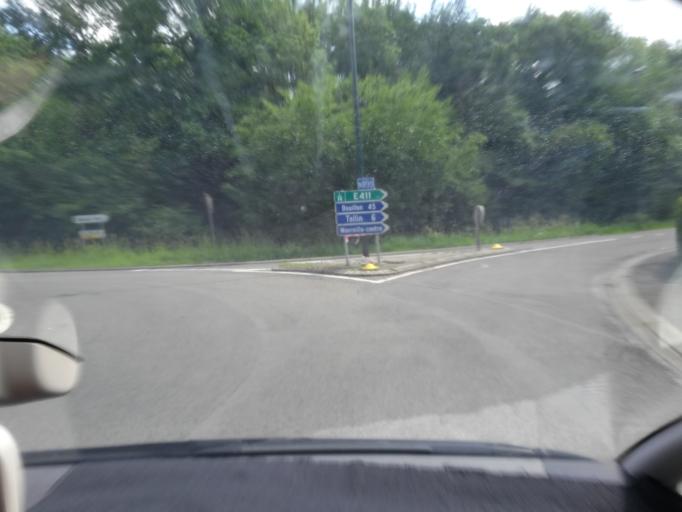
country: BE
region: Wallonia
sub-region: Province de Namur
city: Rochefort
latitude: 50.1233
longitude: 5.2535
